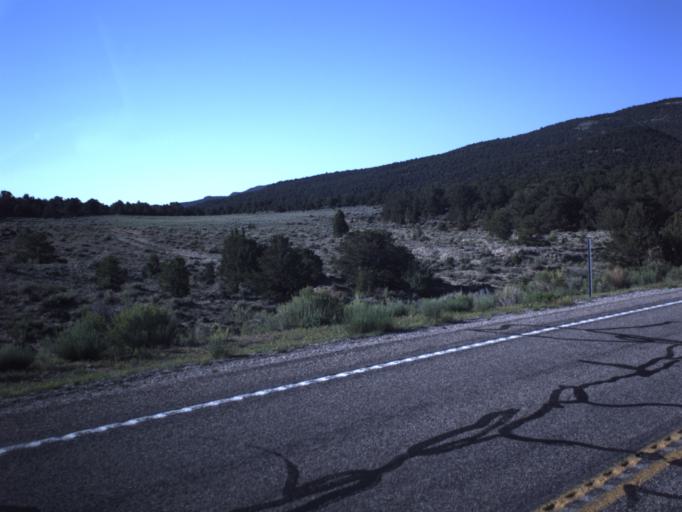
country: US
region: Utah
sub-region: Wayne County
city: Loa
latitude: 38.6765
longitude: -111.4016
